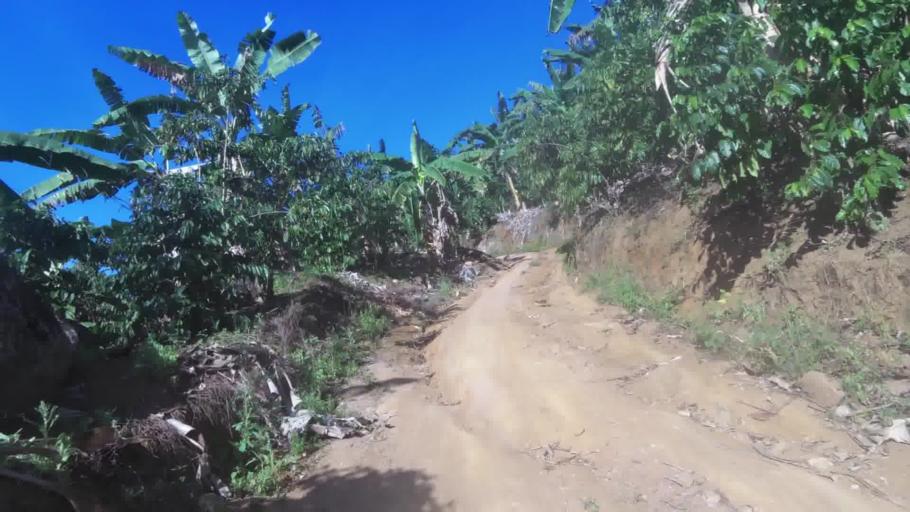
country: BR
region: Espirito Santo
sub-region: Iconha
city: Iconha
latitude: -20.7551
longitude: -40.8113
